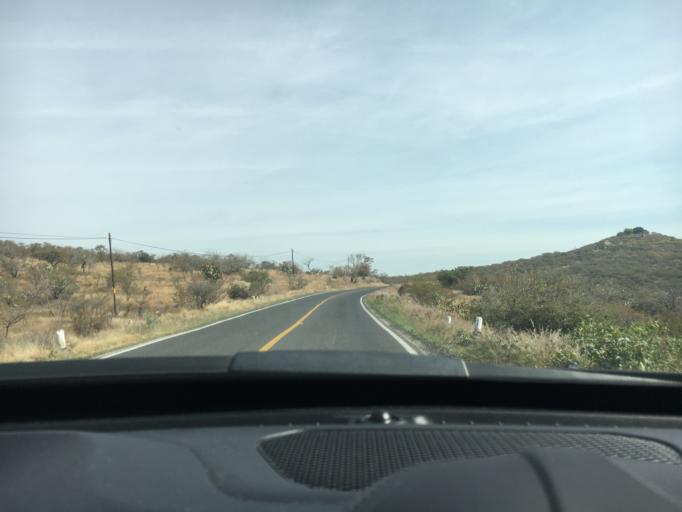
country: MX
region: Guanajuato
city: Duarte
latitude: 21.0623
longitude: -101.5031
